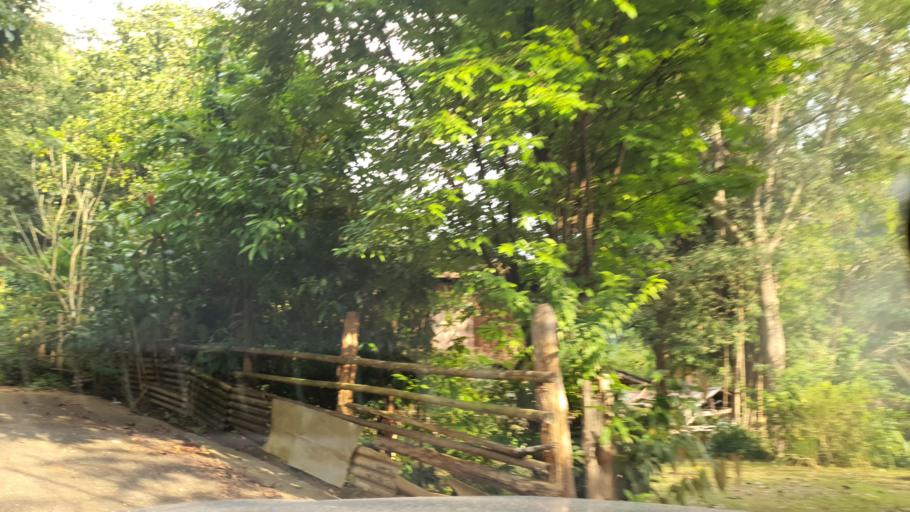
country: TH
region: Chiang Mai
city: Mae On
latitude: 18.8914
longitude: 99.2653
